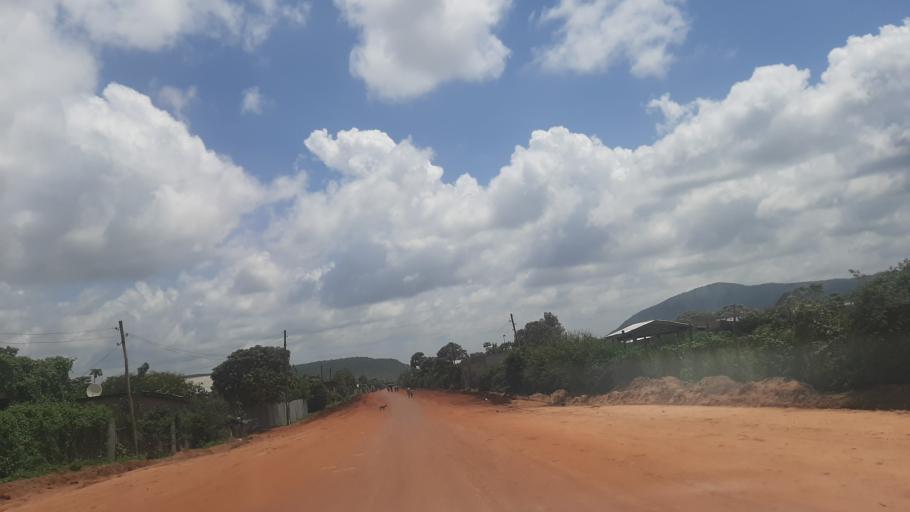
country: ET
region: Oromiya
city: Yabelo
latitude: 4.8936
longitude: 38.1026
